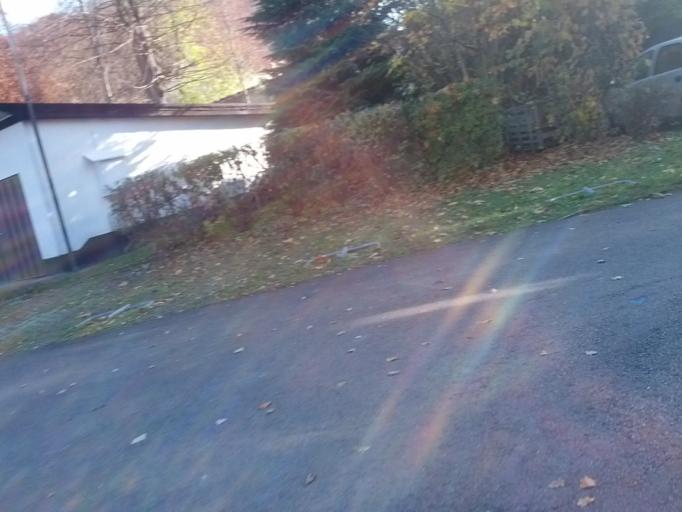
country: DE
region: Thuringia
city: Thal
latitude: 50.9162
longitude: 10.3918
